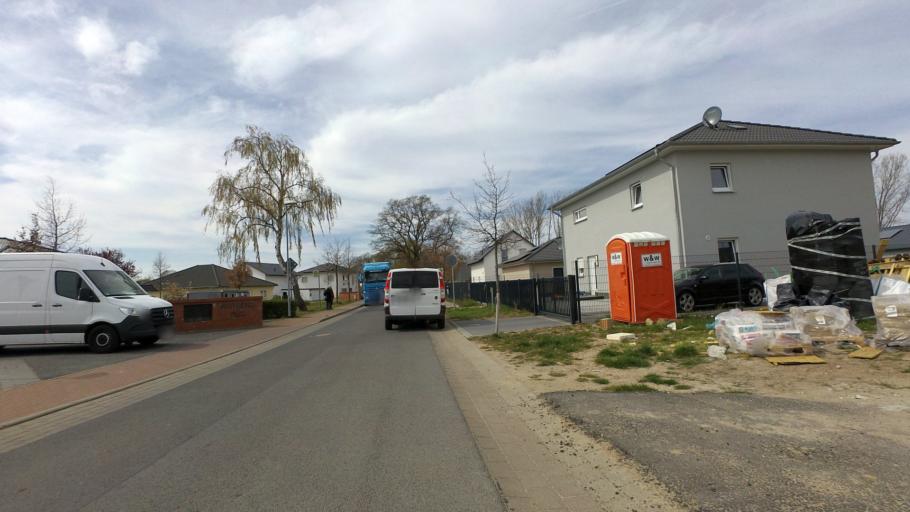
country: DE
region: Brandenburg
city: Schonefeld
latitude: 52.3393
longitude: 13.5254
